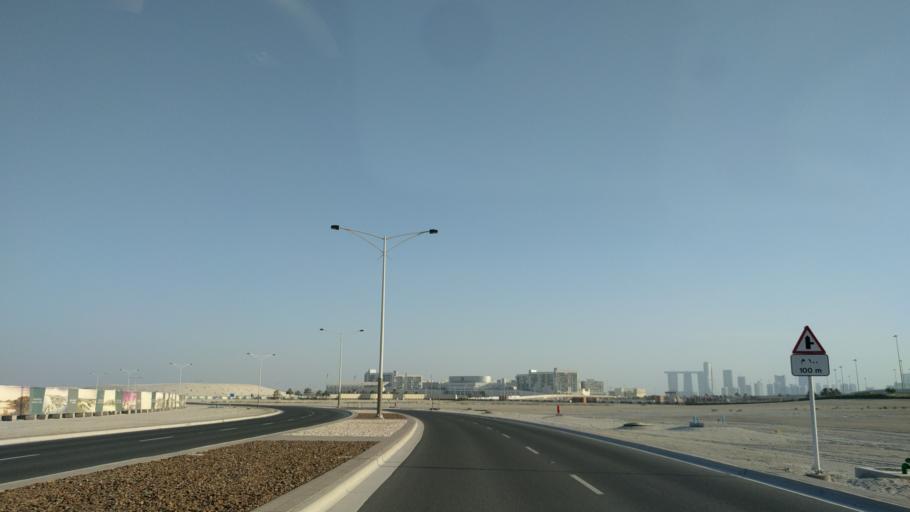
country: AE
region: Abu Dhabi
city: Abu Dhabi
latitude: 24.5367
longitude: 54.4384
